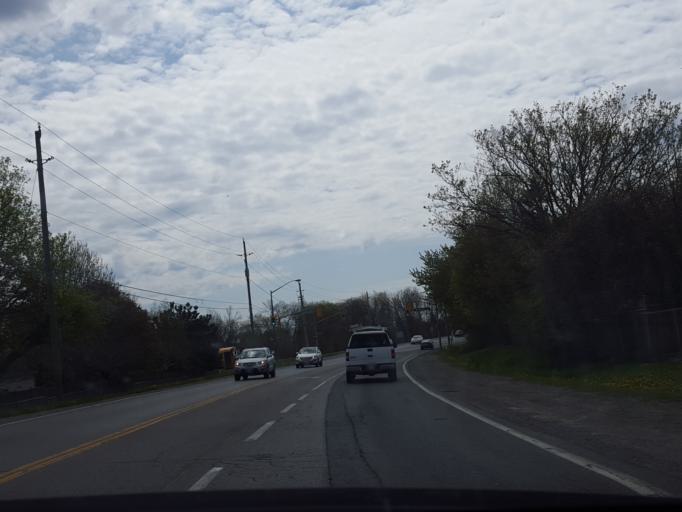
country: CA
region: Ontario
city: Oshawa
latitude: 43.9010
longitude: -78.6939
